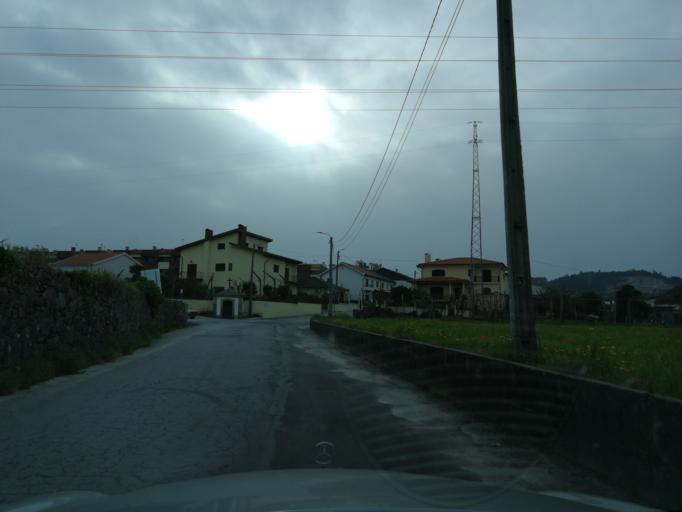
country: PT
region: Braga
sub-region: Braga
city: Adaufe
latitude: 41.5833
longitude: -8.4329
